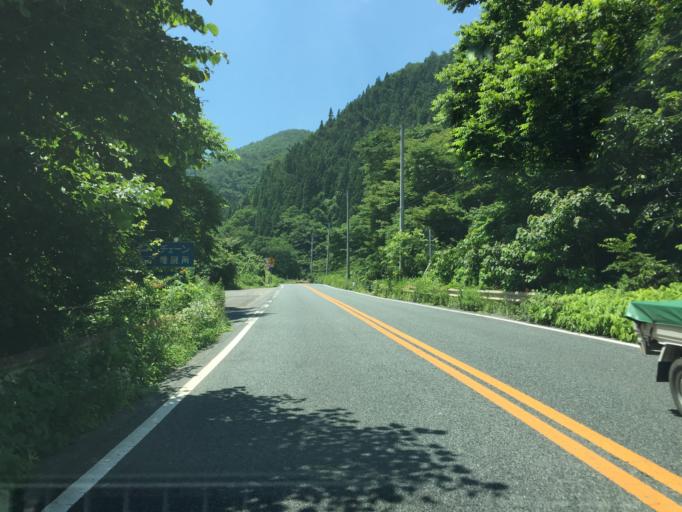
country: JP
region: Miyagi
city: Marumori
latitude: 37.7782
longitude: 140.8007
